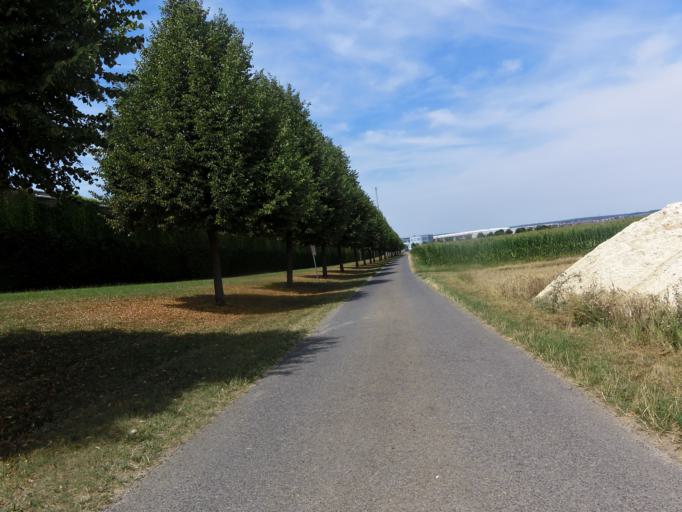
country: DE
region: Bavaria
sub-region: Regierungsbezirk Unterfranken
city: Rottendorf
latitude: 49.7979
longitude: 10.0072
